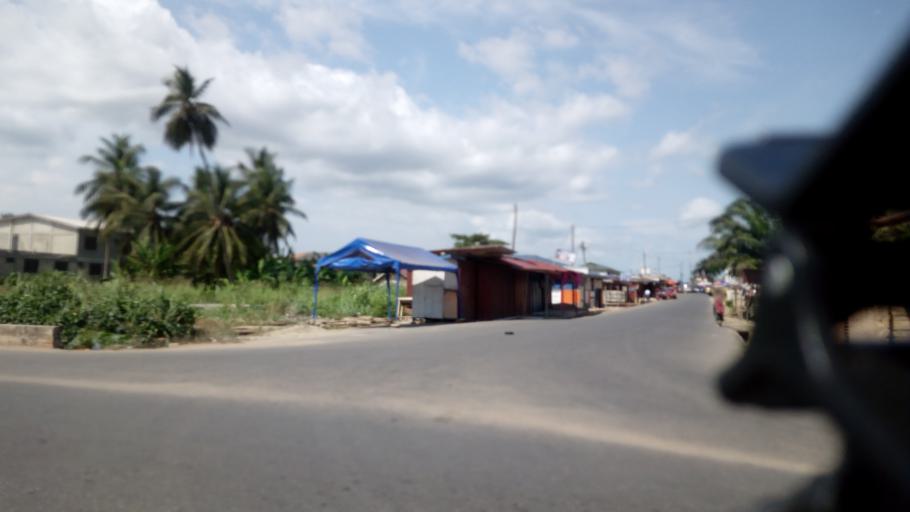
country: GH
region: Central
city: Cape Coast
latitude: 5.1323
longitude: -1.2777
